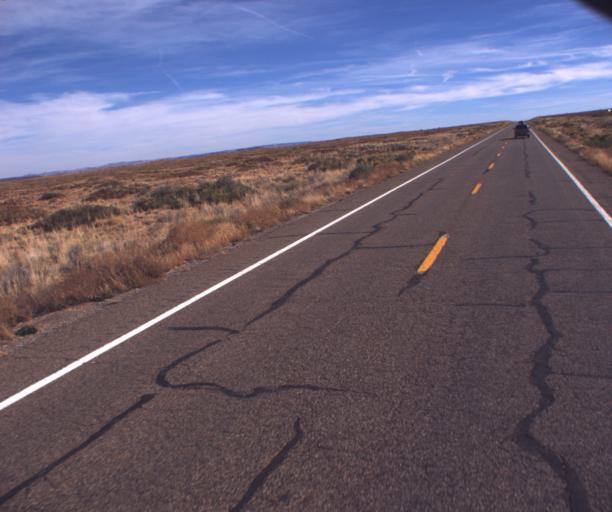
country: US
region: Arizona
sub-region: Coconino County
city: Kaibito
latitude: 36.6128
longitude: -111.0091
